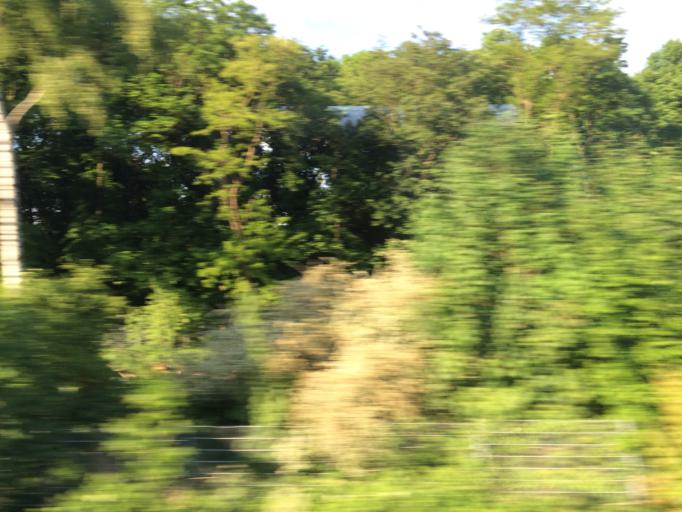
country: DE
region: North Rhine-Westphalia
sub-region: Regierungsbezirk Dusseldorf
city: Erkrath
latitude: 51.1905
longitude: 6.8495
